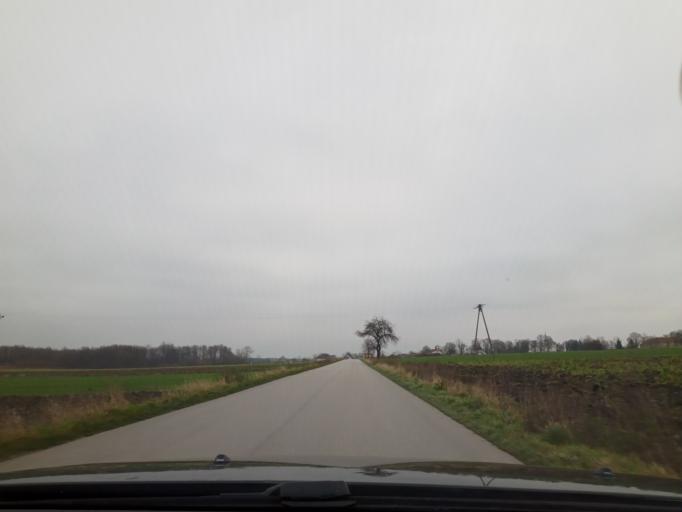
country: PL
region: Swietokrzyskie
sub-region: Powiat jedrzejowski
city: Imielno
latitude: 50.5886
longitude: 20.4370
